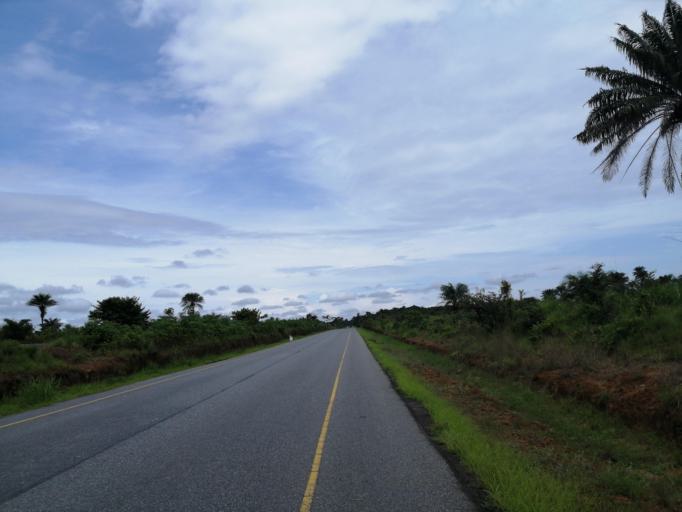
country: SL
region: Northern Province
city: Port Loko
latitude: 8.7458
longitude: -12.9241
